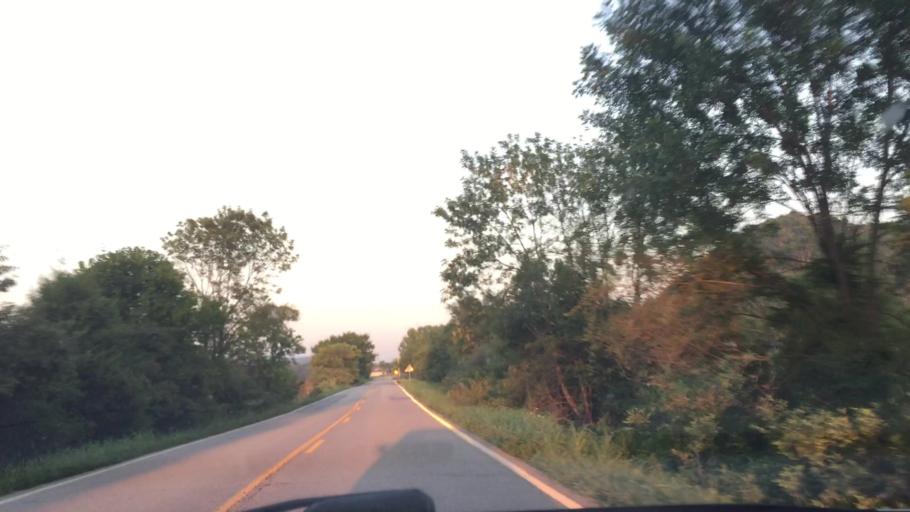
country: US
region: Kentucky
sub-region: Carroll County
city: Carrollton
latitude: 38.6451
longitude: -85.1511
